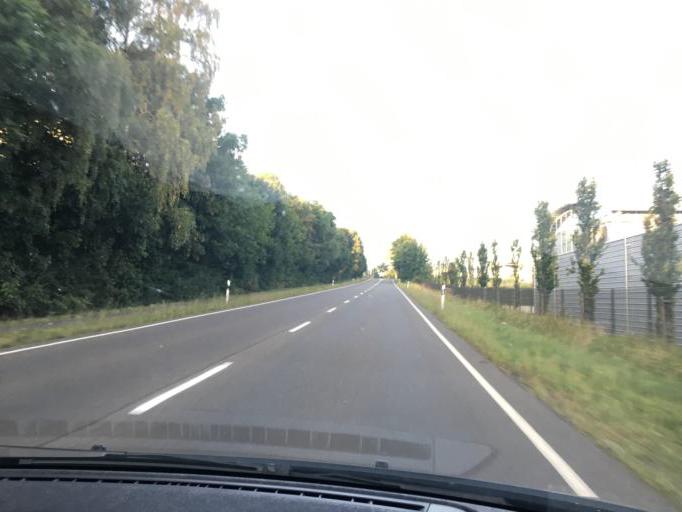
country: DE
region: North Rhine-Westphalia
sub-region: Regierungsbezirk Koln
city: Monschau
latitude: 50.5798
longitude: 6.2671
